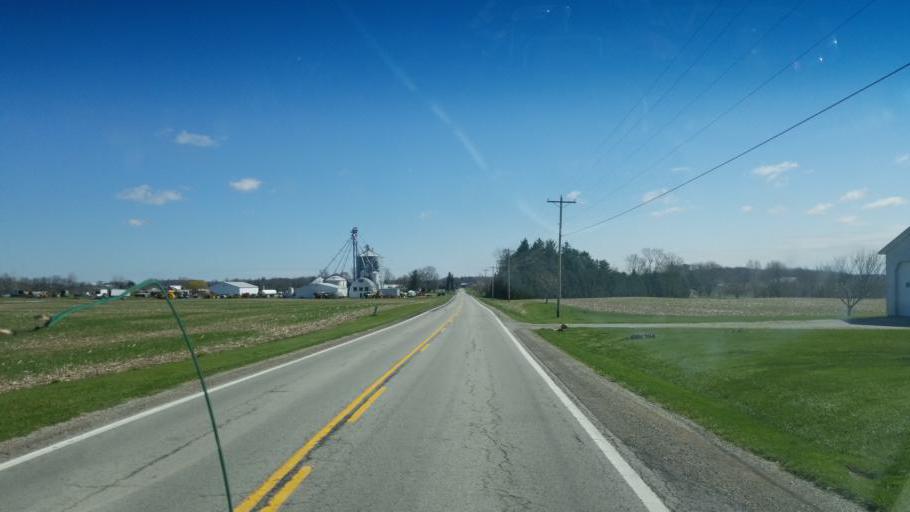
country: US
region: Ohio
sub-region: Crawford County
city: Bucyrus
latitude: 40.8795
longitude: -82.8623
